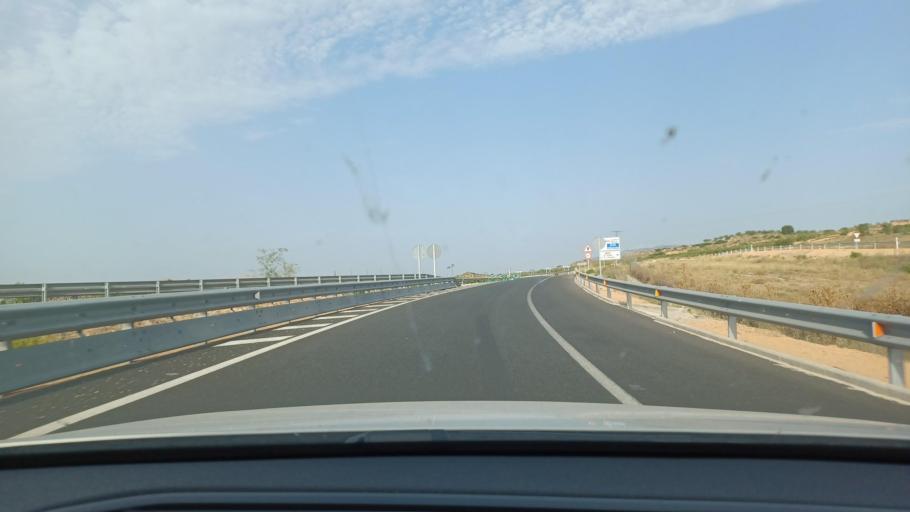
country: ES
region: Valencia
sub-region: Provincia de Valencia
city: La Font de la Figuera
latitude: 38.7455
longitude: -0.9195
